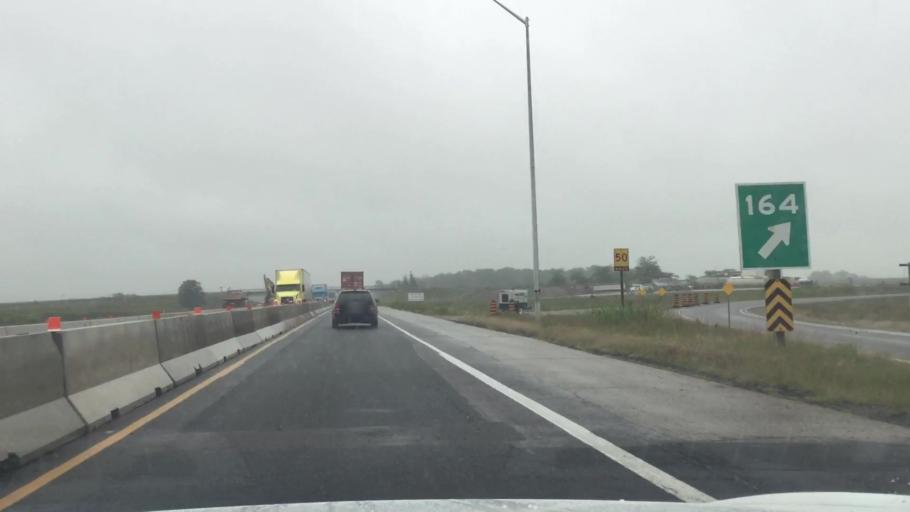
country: CA
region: Ontario
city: Delaware
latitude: 42.7696
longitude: -81.3831
